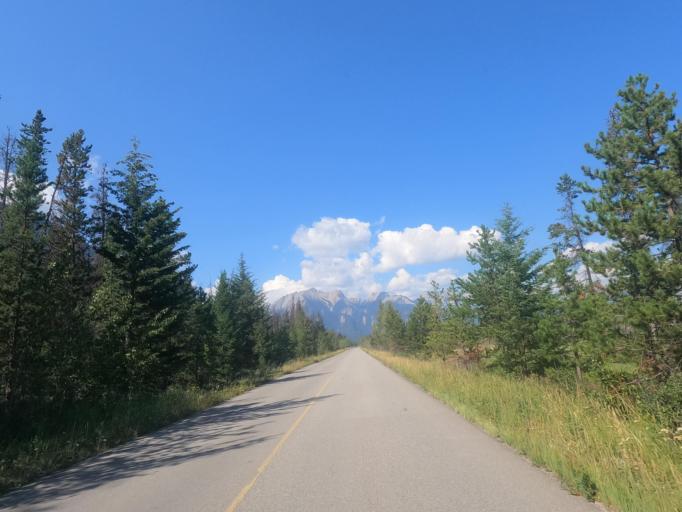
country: CA
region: Alberta
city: Jasper Park Lodge
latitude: 52.9778
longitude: -118.0678
